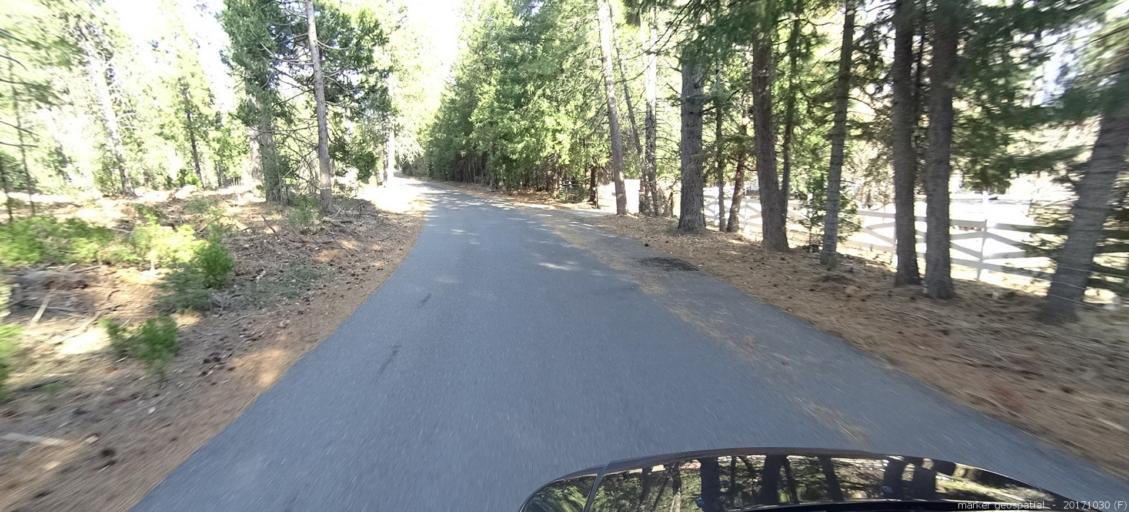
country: US
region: California
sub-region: Shasta County
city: Shingletown
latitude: 40.5094
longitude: -121.7351
